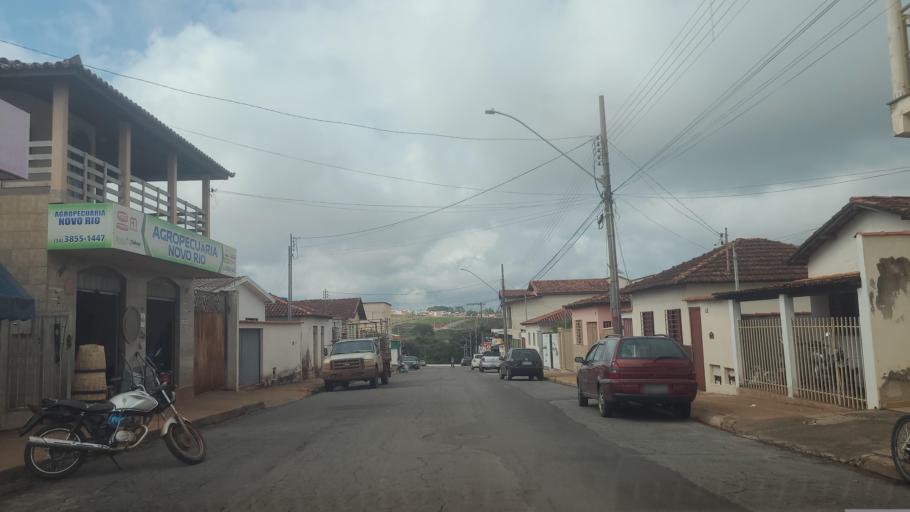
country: BR
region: Minas Gerais
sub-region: Carmo Do Paranaiba
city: Carmo do Paranaiba
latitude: -19.1935
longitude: -46.2448
